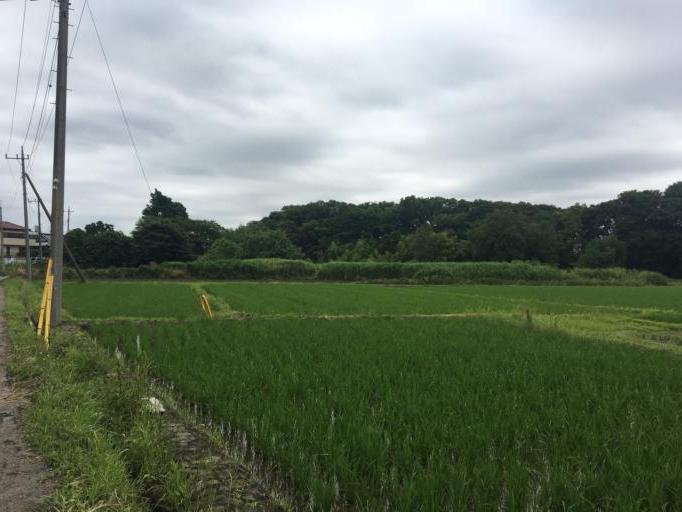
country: JP
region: Saitama
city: Okegawa
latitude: 35.9416
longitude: 139.5467
